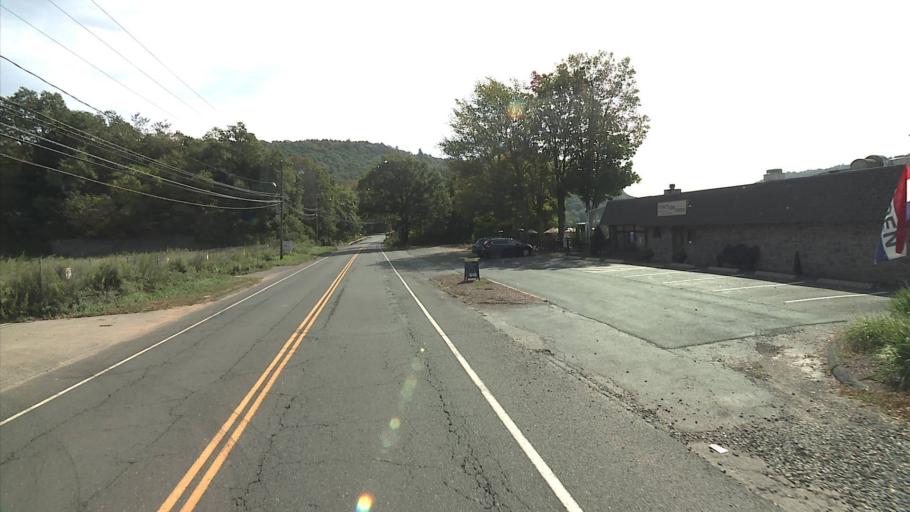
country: US
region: Connecticut
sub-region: New Haven County
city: Ansonia
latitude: 41.3652
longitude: -73.1421
